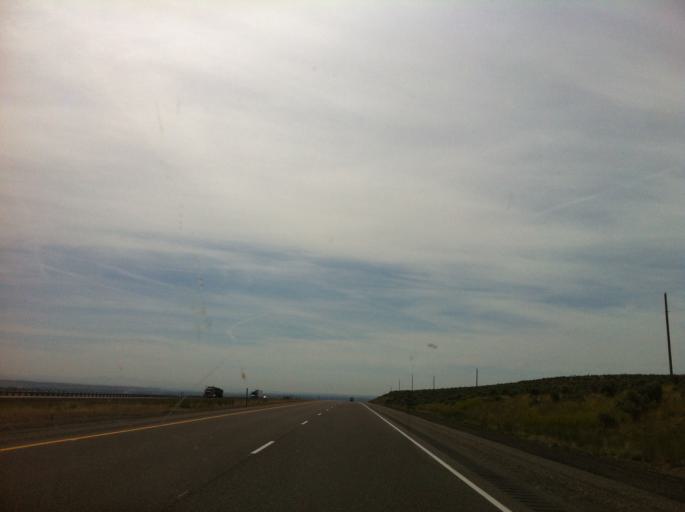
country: US
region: Oregon
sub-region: Malheur County
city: Ontario
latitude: 44.1158
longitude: -117.0622
